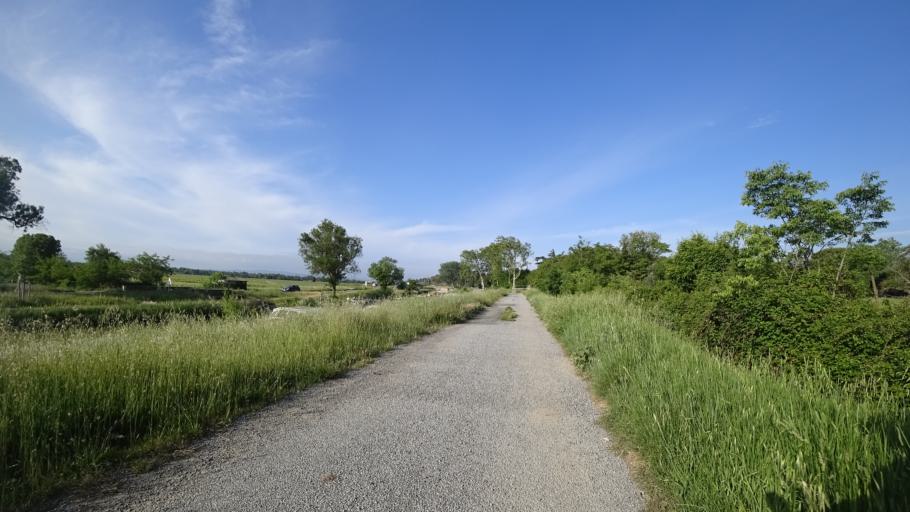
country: FR
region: Languedoc-Roussillon
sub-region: Departement de l'Aude
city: Canet
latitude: 43.2479
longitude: 2.8044
